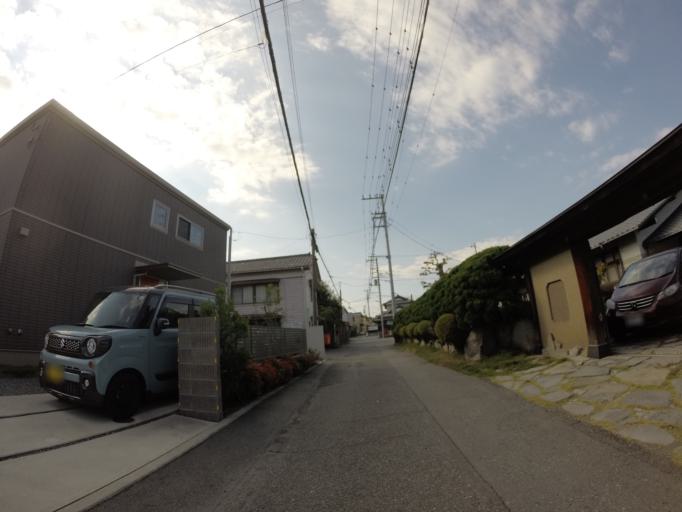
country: JP
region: Shizuoka
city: Fuji
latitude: 35.1345
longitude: 138.6805
